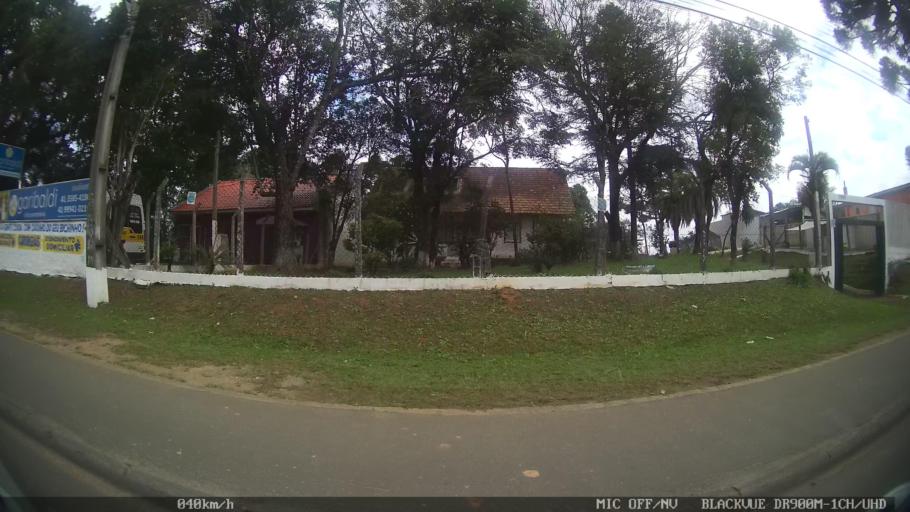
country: BR
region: Parana
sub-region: Almirante Tamandare
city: Almirante Tamandare
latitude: -25.3574
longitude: -49.2638
